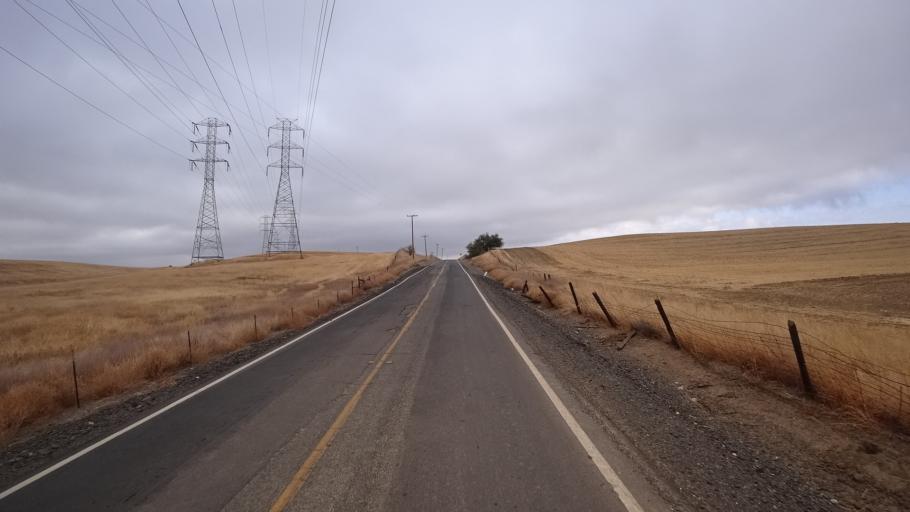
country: US
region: California
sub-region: Yolo County
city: Dunnigan
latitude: 38.8275
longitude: -122.0433
